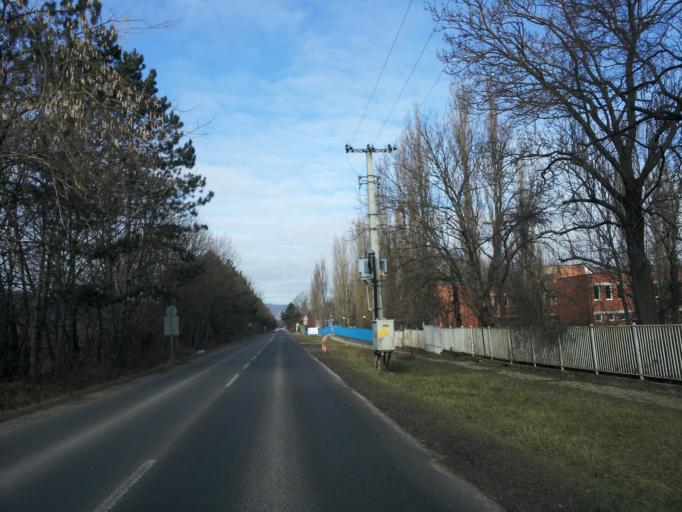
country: HU
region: Pest
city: Budakeszi
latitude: 47.5487
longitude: 18.9355
